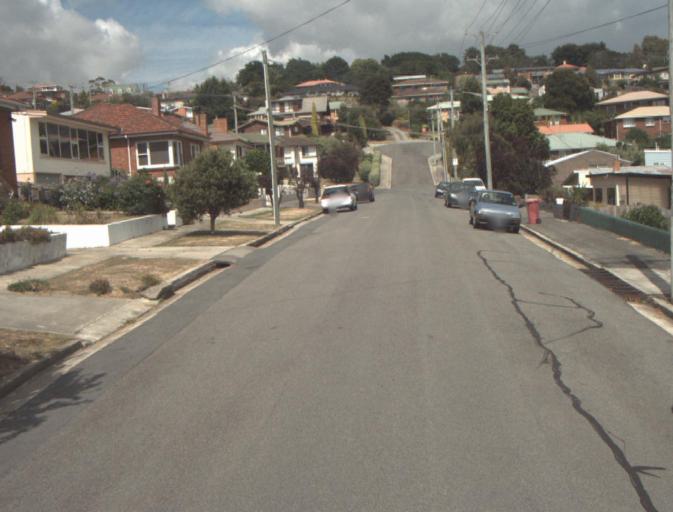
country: AU
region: Tasmania
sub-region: Launceston
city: Summerhill
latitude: -41.4678
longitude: 147.1520
